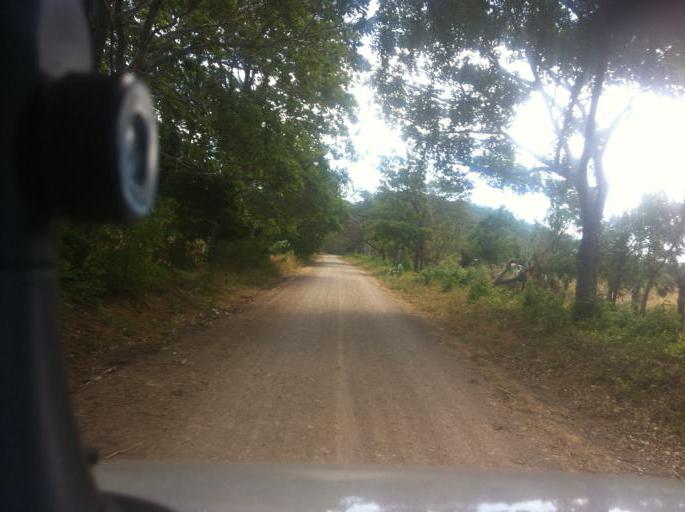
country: NI
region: Rivas
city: Belen
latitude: 11.5868
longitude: -86.0248
